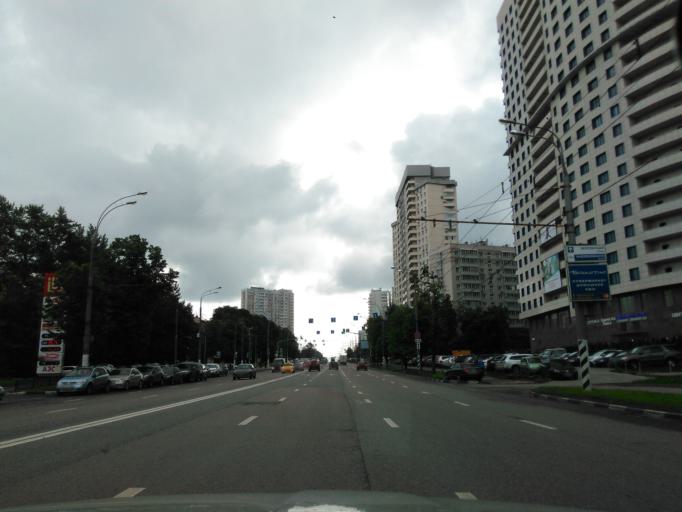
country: RU
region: Moskovskaya
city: Cheremushki
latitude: 55.6602
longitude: 37.5605
